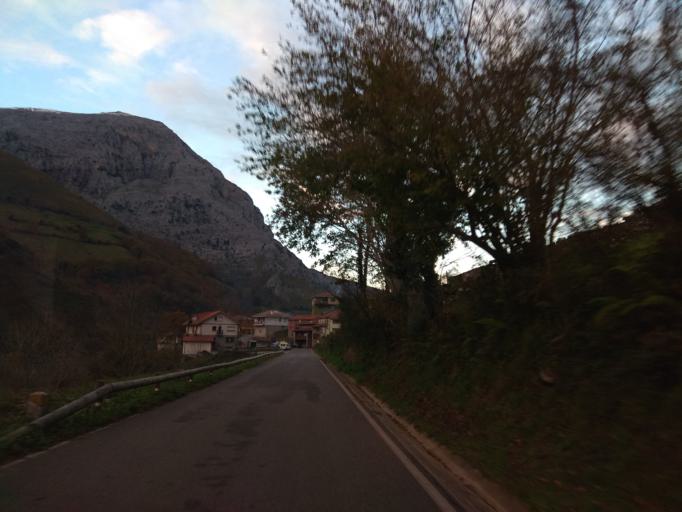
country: ES
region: Cantabria
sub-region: Provincia de Cantabria
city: Arredondo
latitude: 43.2384
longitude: -3.6056
